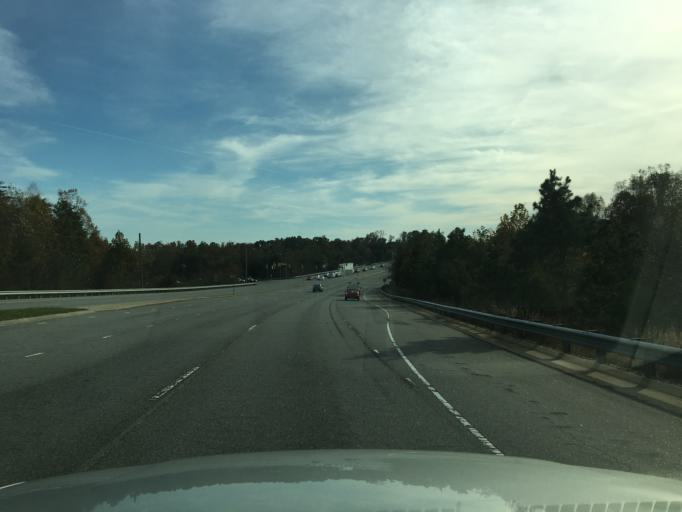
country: US
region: North Carolina
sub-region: Catawba County
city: Saint Stephens
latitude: 35.7282
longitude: -81.2906
